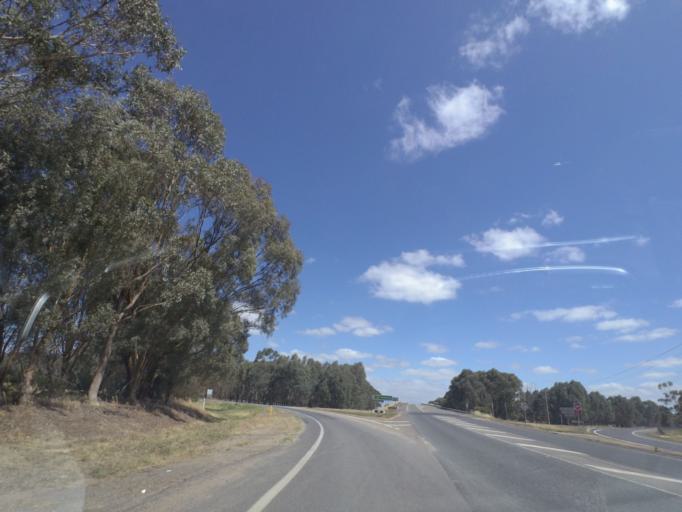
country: AU
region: Victoria
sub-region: Wangaratta
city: Wangaratta
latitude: -36.4015
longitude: 146.2987
